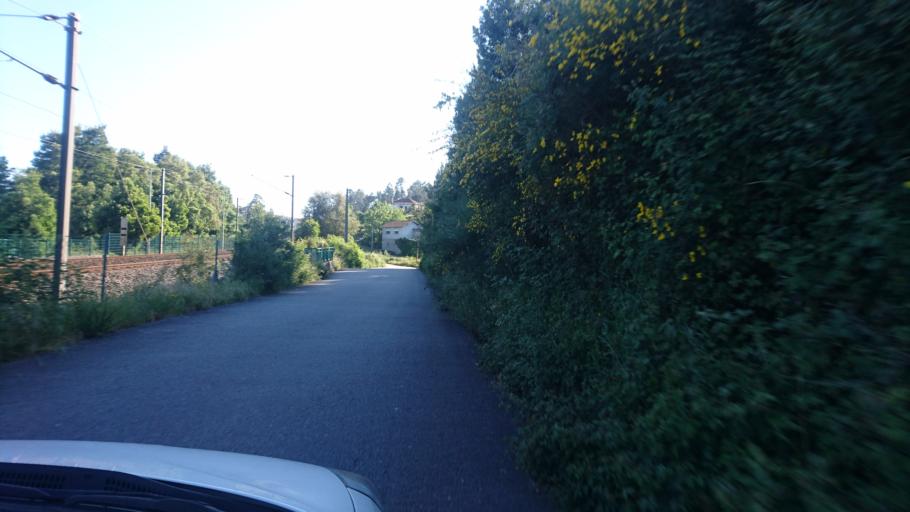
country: PT
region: Porto
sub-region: Paredes
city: Recarei
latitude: 41.1558
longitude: -8.3836
